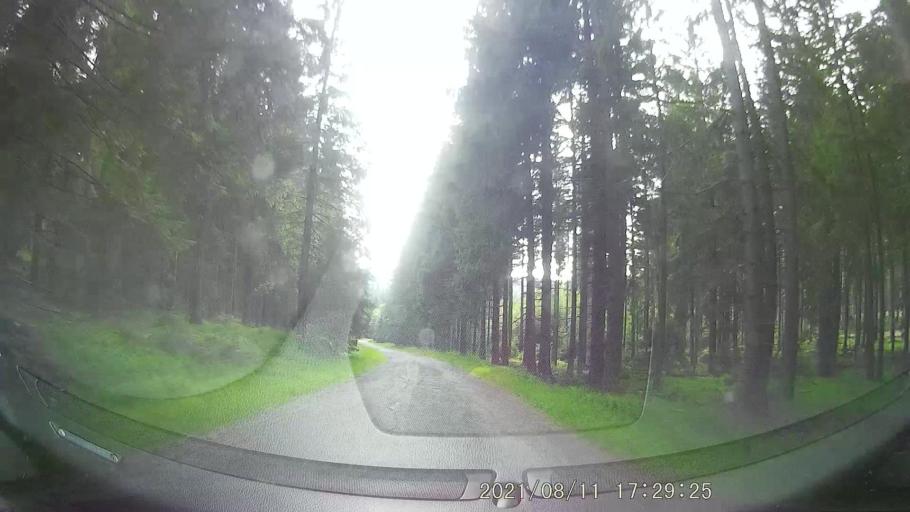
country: PL
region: Lower Silesian Voivodeship
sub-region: Powiat klodzki
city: Polanica-Zdroj
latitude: 50.2986
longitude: 16.4751
